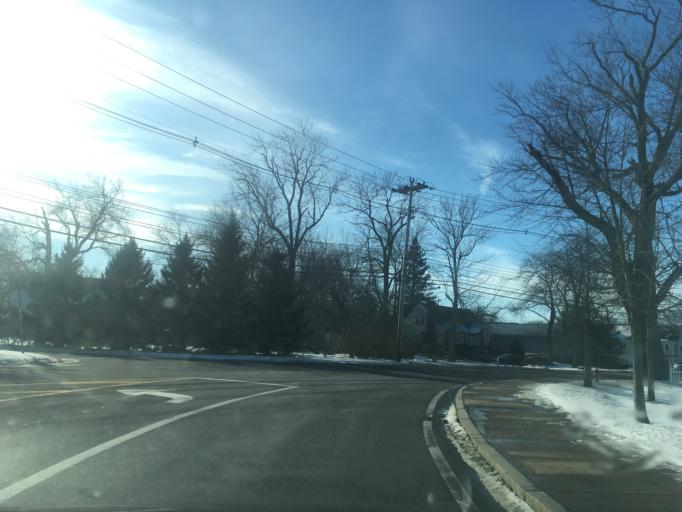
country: US
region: Massachusetts
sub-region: Essex County
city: Salisbury
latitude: 42.8397
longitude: -70.8625
